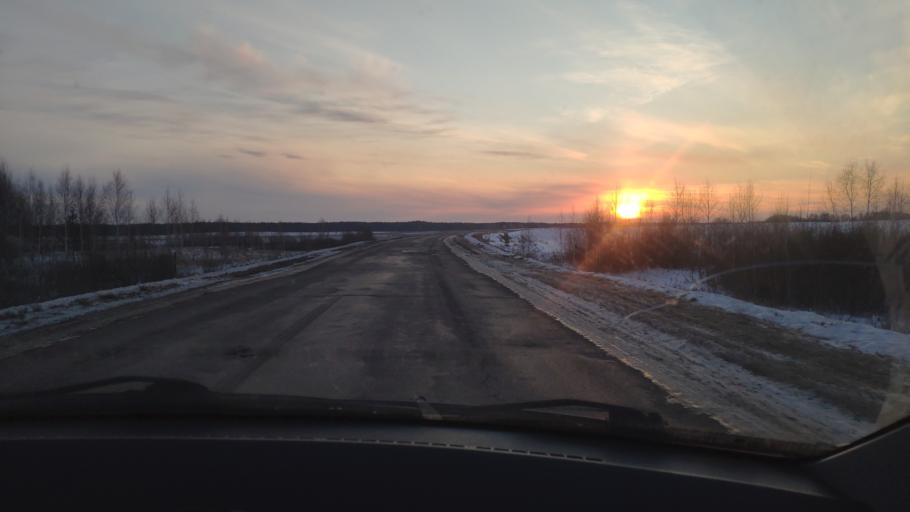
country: RU
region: Kurgan
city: Kataysk
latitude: 55.8897
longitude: 62.5359
